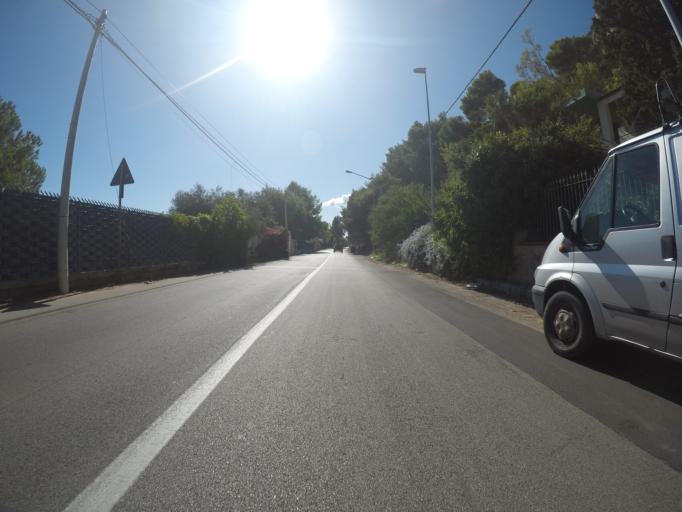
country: IT
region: Sicily
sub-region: Palermo
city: Palermo
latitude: 38.1829
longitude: 13.3645
